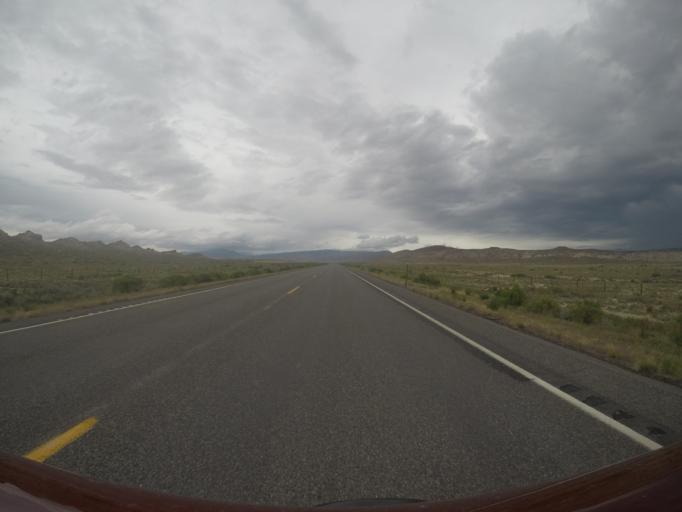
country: US
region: Wyoming
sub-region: Big Horn County
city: Lovell
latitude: 44.9073
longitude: -108.2911
